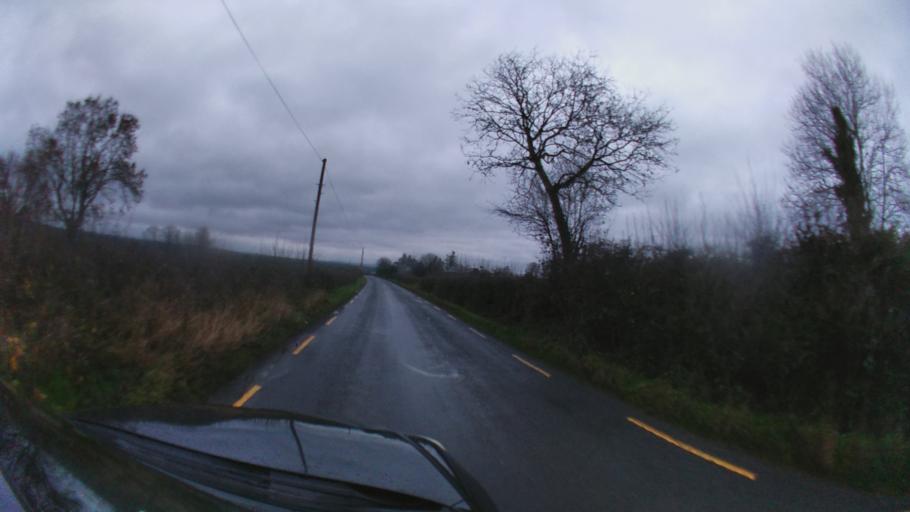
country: IE
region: Leinster
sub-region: Kilkenny
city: Graiguenamanagh
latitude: 52.5978
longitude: -6.9898
